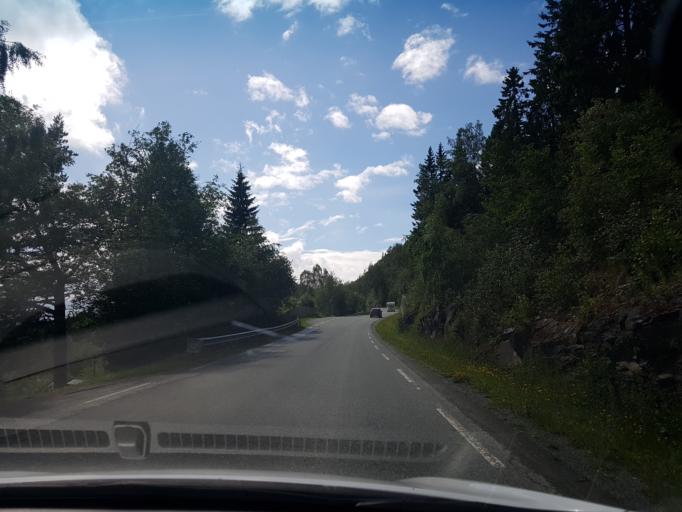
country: NO
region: Nord-Trondelag
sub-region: Frosta
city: Frosta
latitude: 63.5997
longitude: 10.8586
